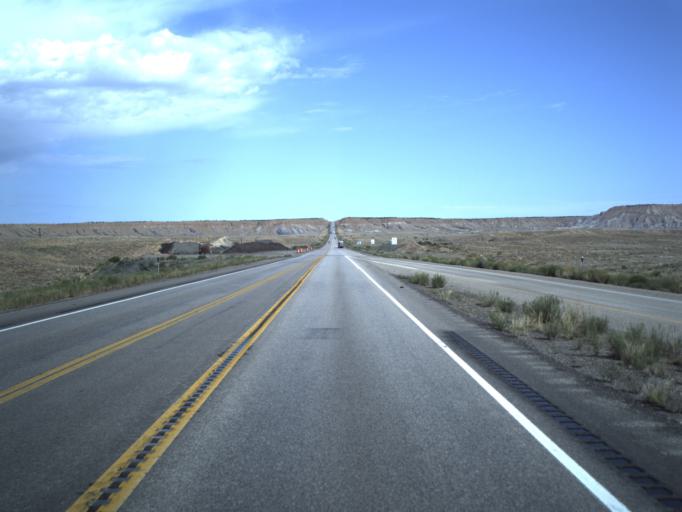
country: US
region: Utah
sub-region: Carbon County
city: East Carbon City
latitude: 39.3727
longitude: -110.3991
